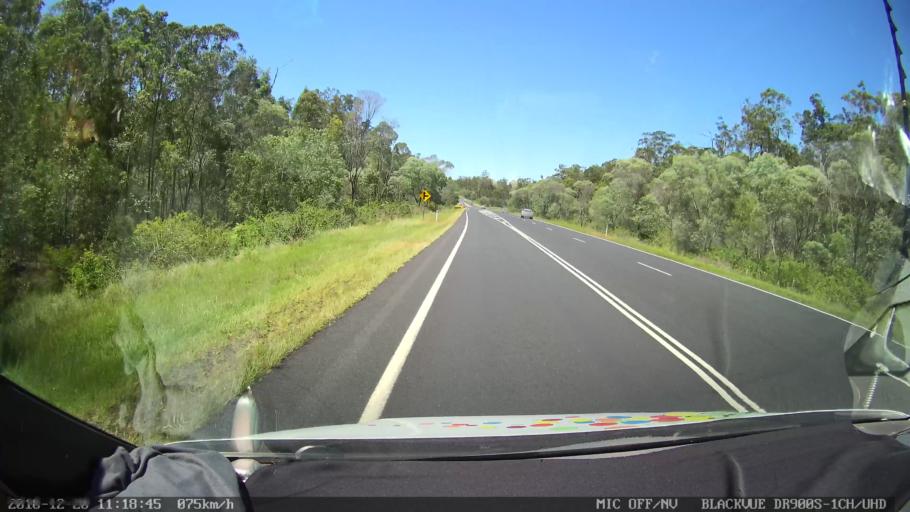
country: AU
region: New South Wales
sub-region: Richmond Valley
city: Casino
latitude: -29.0550
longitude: 153.0060
